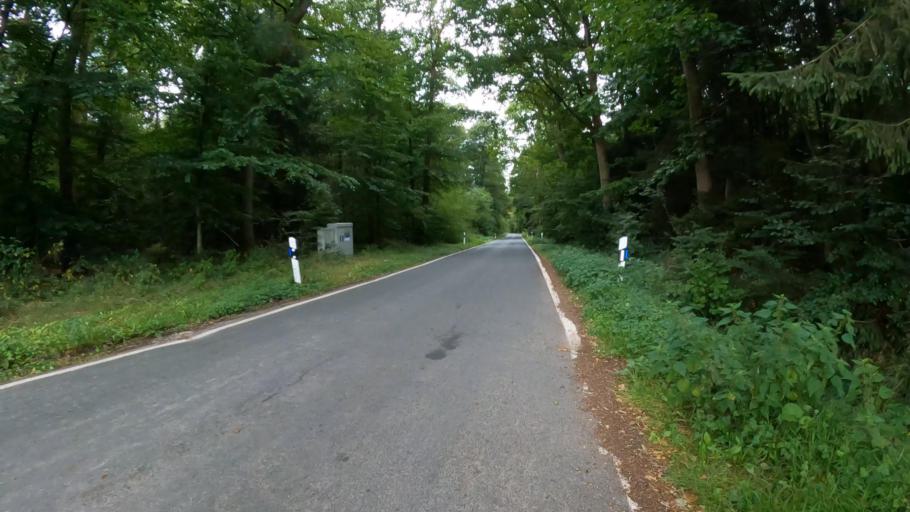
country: DE
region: Lower Saxony
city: Kakenstorf
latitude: 53.3239
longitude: 9.7533
